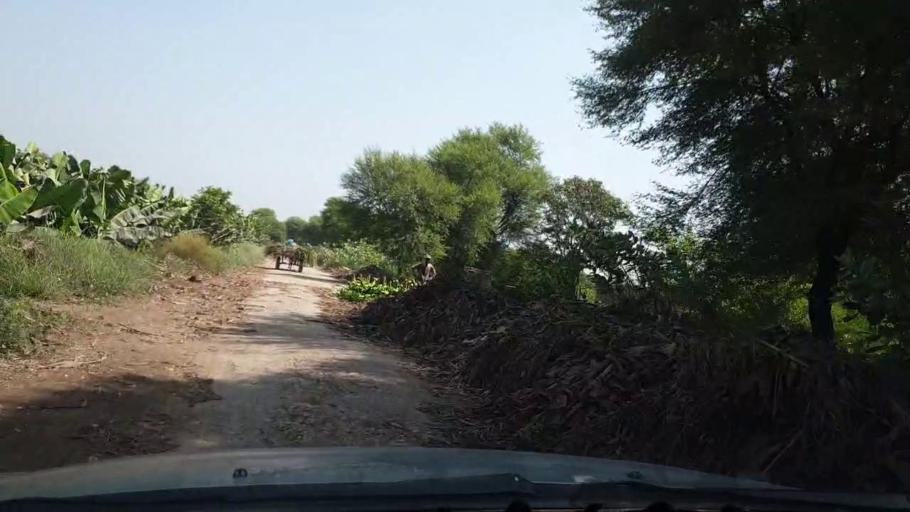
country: PK
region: Sindh
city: Matli
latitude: 25.1754
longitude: 68.6601
